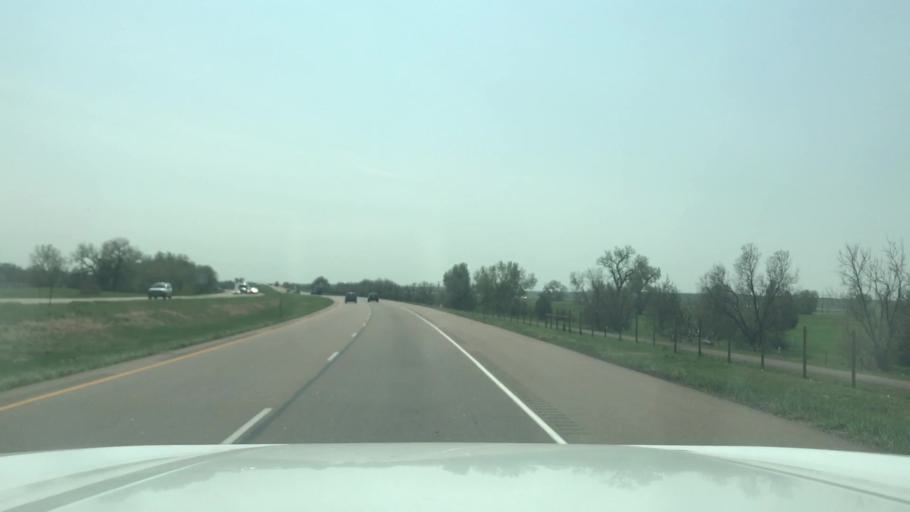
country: US
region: Colorado
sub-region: El Paso County
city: Fountain
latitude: 38.6171
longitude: -104.6881
